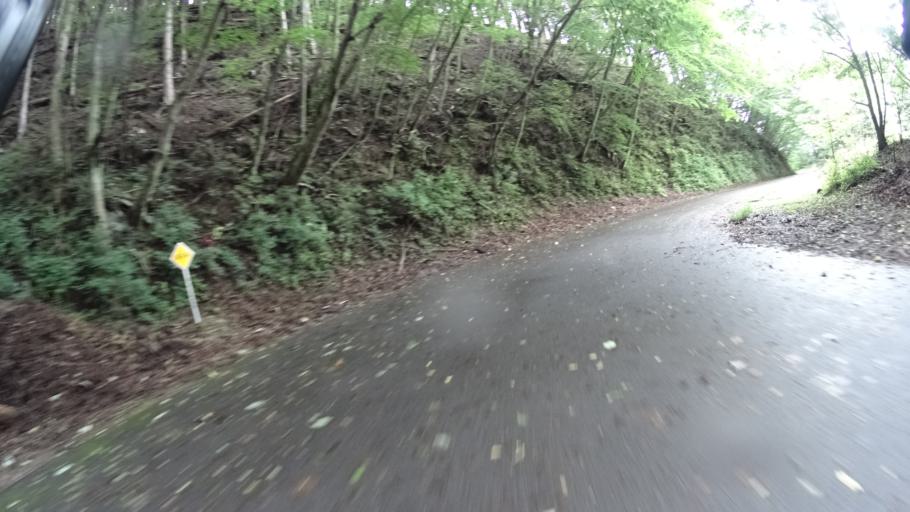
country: JP
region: Saitama
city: Chichibu
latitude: 35.8863
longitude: 139.1188
